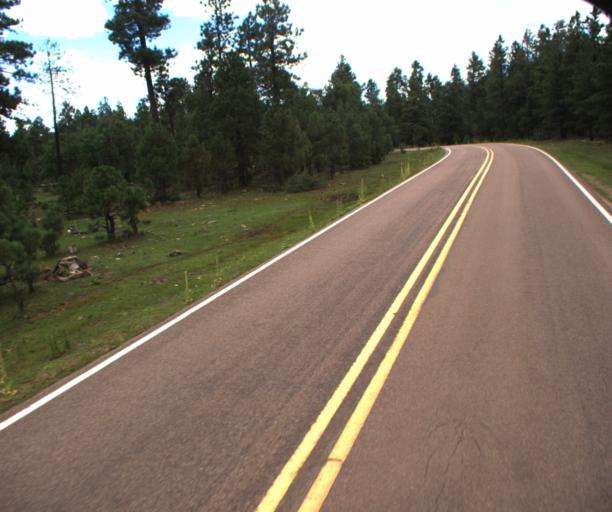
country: US
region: Arizona
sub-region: Navajo County
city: Pinetop-Lakeside
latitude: 34.0119
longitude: -109.7745
